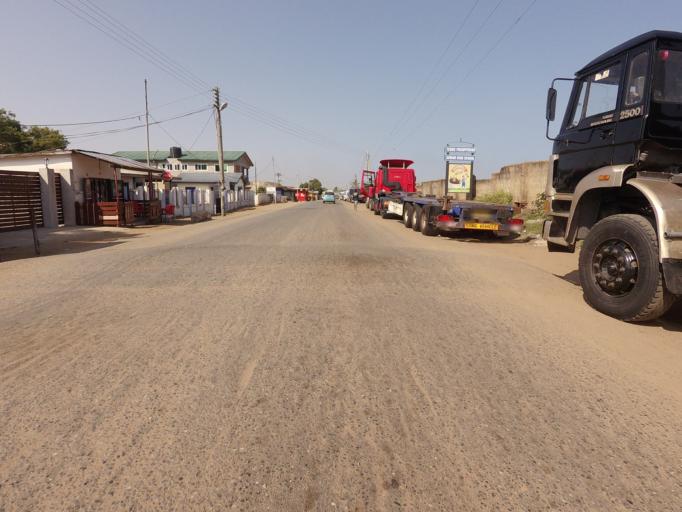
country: GH
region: Greater Accra
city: Teshi Old Town
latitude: 5.5765
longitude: -0.1082
